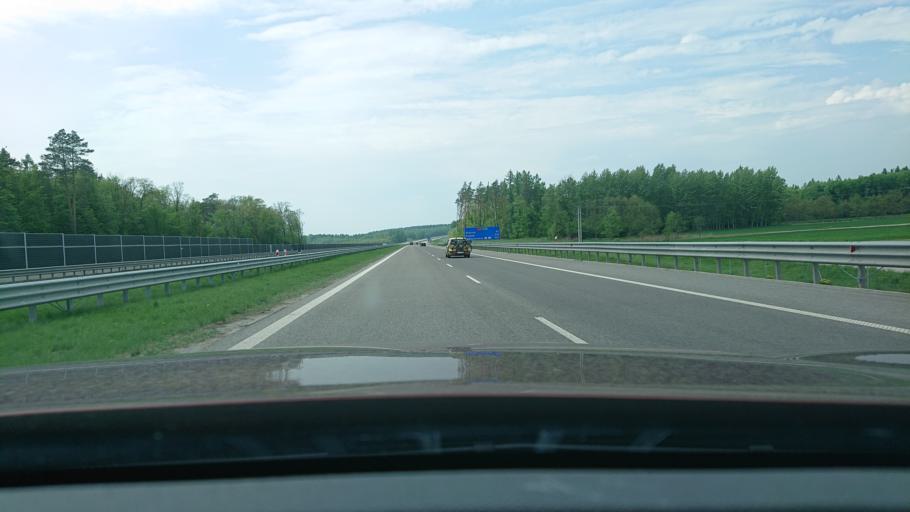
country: PL
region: Subcarpathian Voivodeship
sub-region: Powiat jaroslawski
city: Pawlosiow
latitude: 49.9782
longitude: 22.6314
